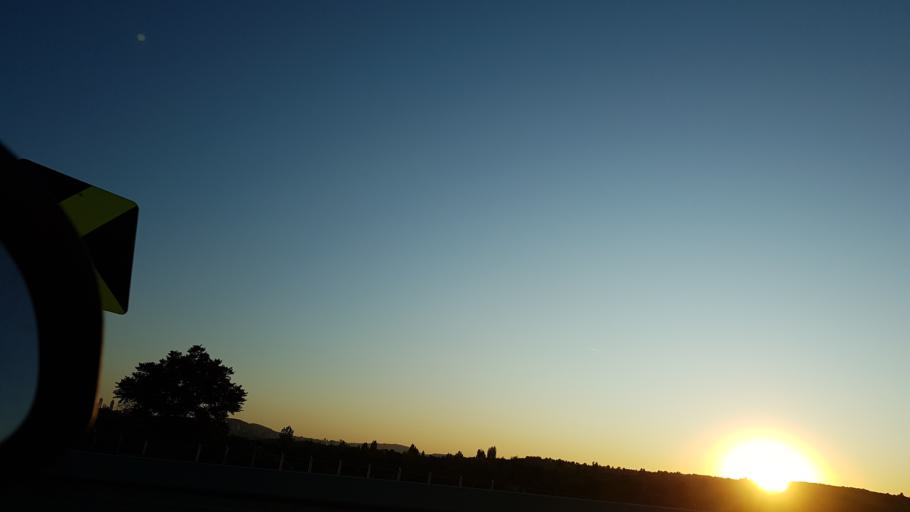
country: TR
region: Ankara
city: Batikent
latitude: 39.9250
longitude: 32.7051
